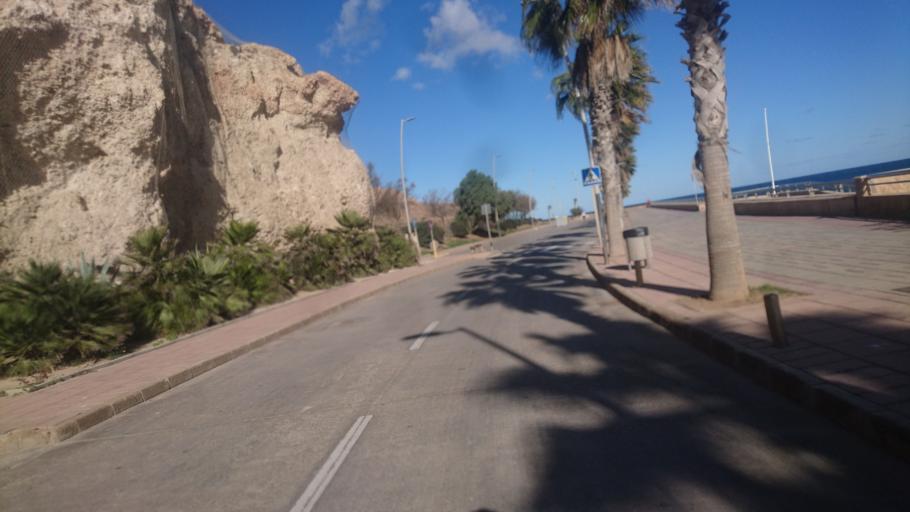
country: ES
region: Melilla
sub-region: Melilla
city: Melilla
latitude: 35.2988
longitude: -2.9370
